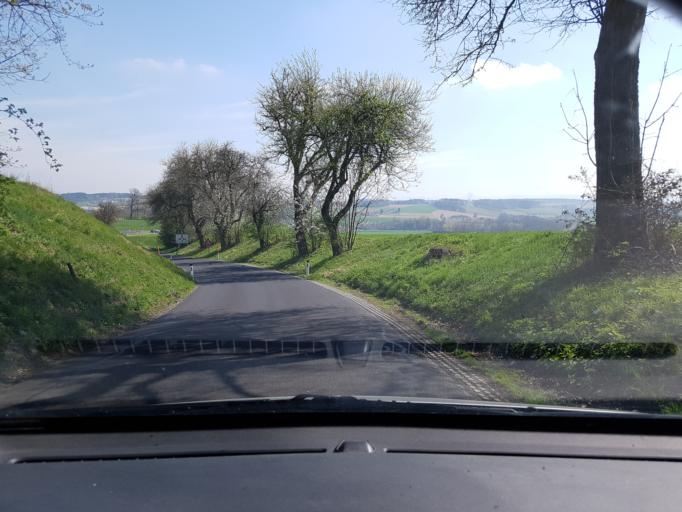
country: AT
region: Upper Austria
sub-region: Politischer Bezirk Linz-Land
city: Sankt Florian
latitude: 48.2059
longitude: 14.3545
